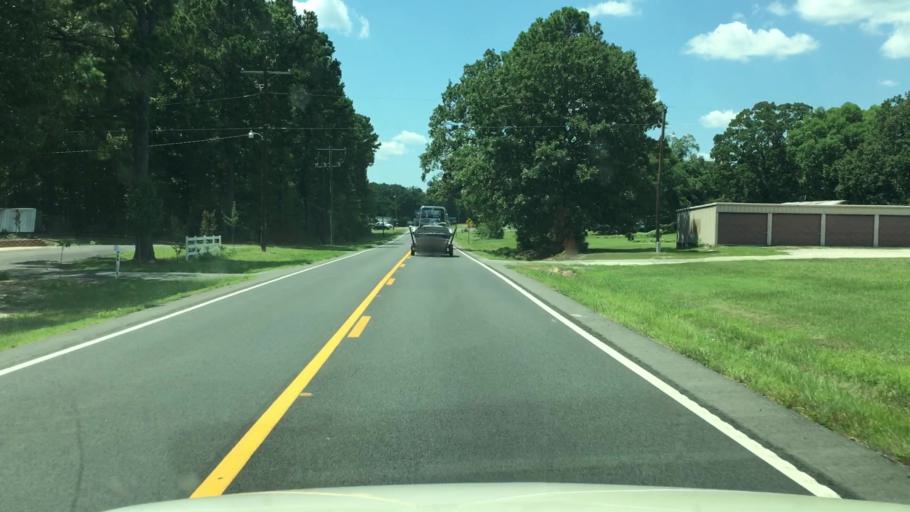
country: US
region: Arkansas
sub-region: Garland County
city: Lake Hamilton
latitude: 34.2671
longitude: -93.1408
